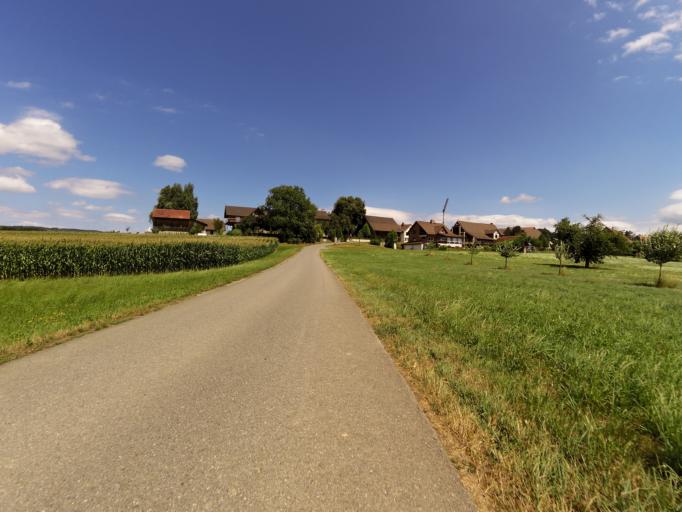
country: CH
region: Thurgau
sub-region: Weinfelden District
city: Wigoltingen
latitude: 47.5989
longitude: 9.0501
